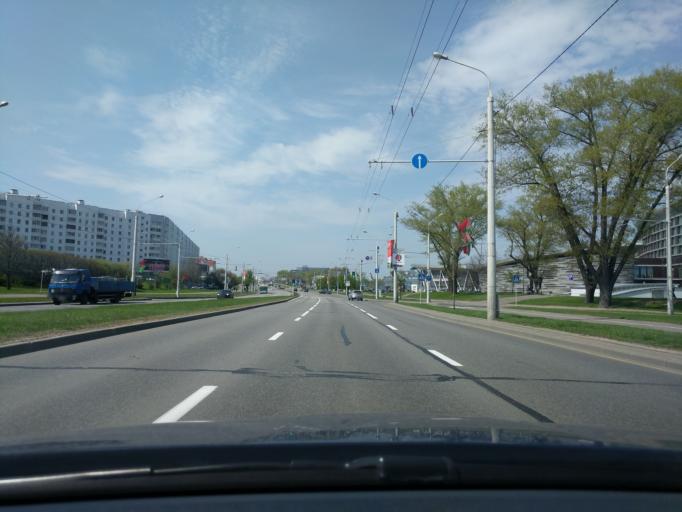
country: BY
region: Minsk
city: Minsk
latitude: 53.9302
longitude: 27.5126
